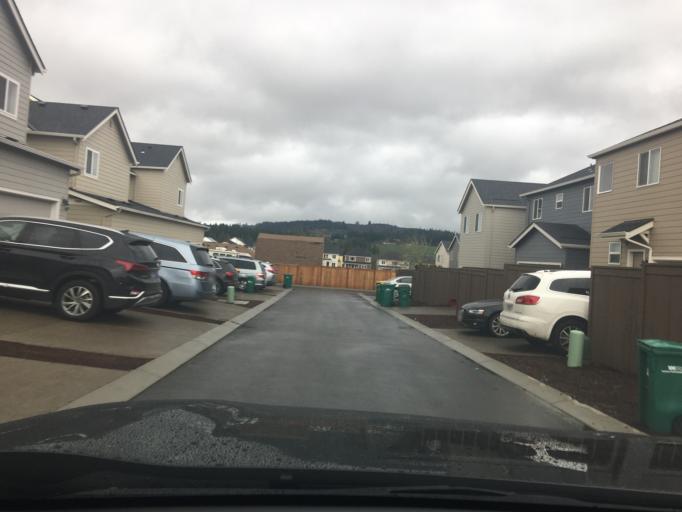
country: US
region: Oregon
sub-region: Washington County
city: Bethany
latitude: 45.5729
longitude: -122.8481
